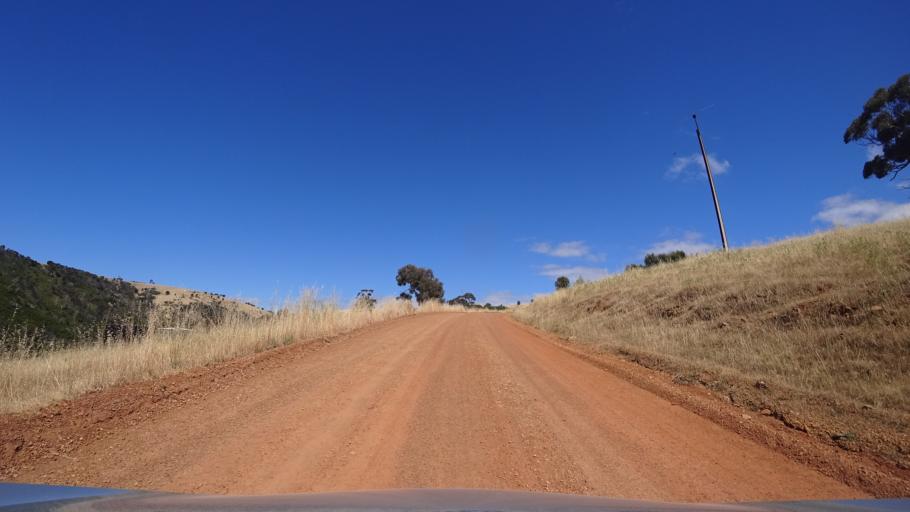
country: AU
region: South Australia
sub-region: Kangaroo Island
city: Kingscote
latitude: -35.6822
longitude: 136.9727
